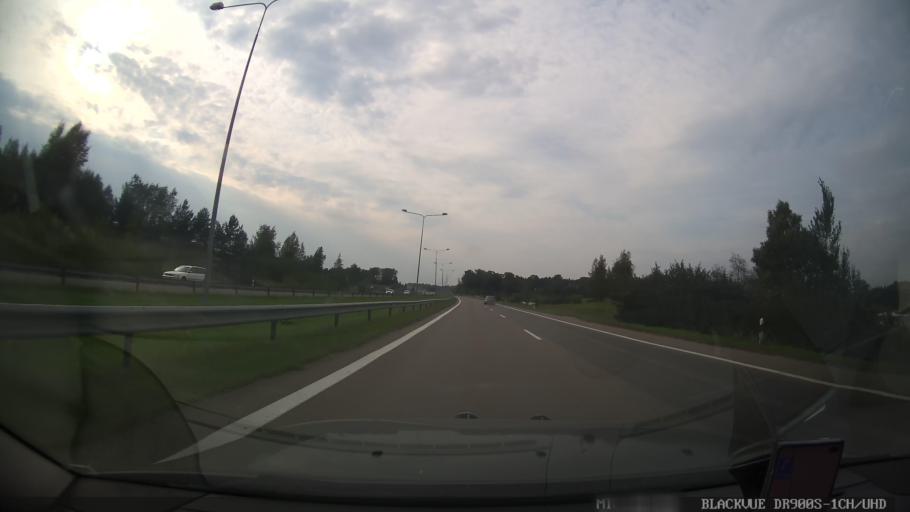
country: LT
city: Skaidiskes
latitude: 54.6345
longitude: 25.3766
